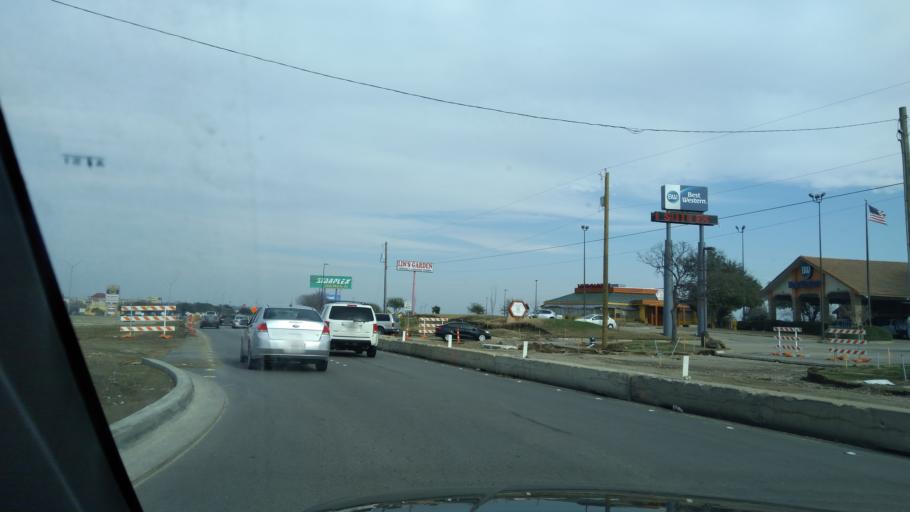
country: US
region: Texas
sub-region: Dallas County
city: Irving
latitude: 32.8363
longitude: -97.0092
